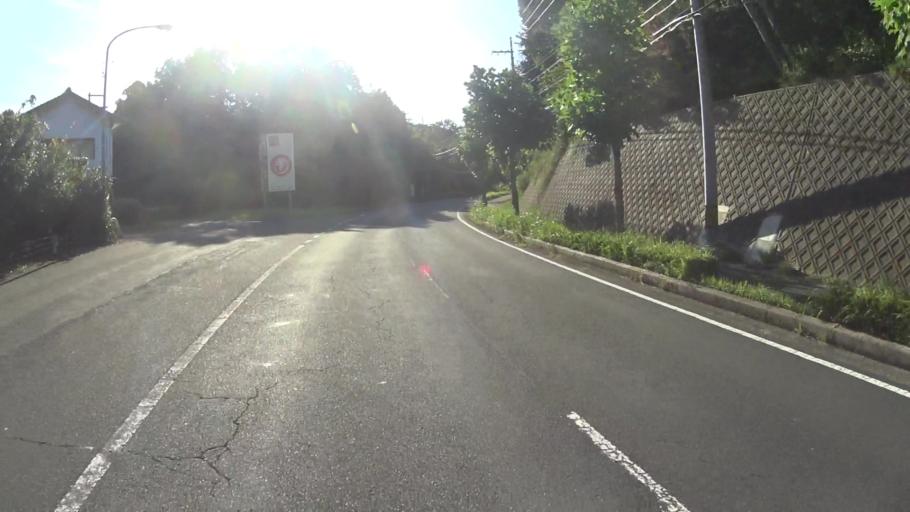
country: JP
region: Hyogo
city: Toyooka
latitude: 35.6350
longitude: 134.9371
